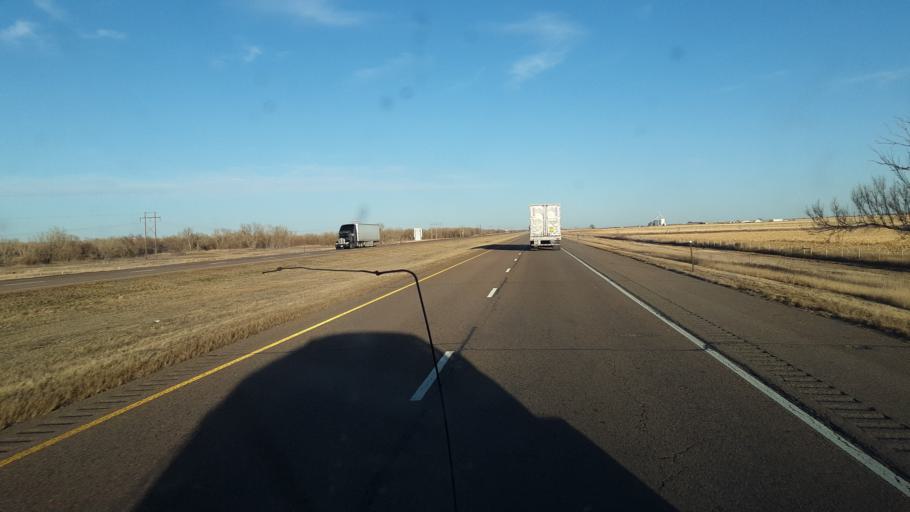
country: US
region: Nebraska
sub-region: Keith County
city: Ogallala
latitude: 41.0829
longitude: -101.8690
